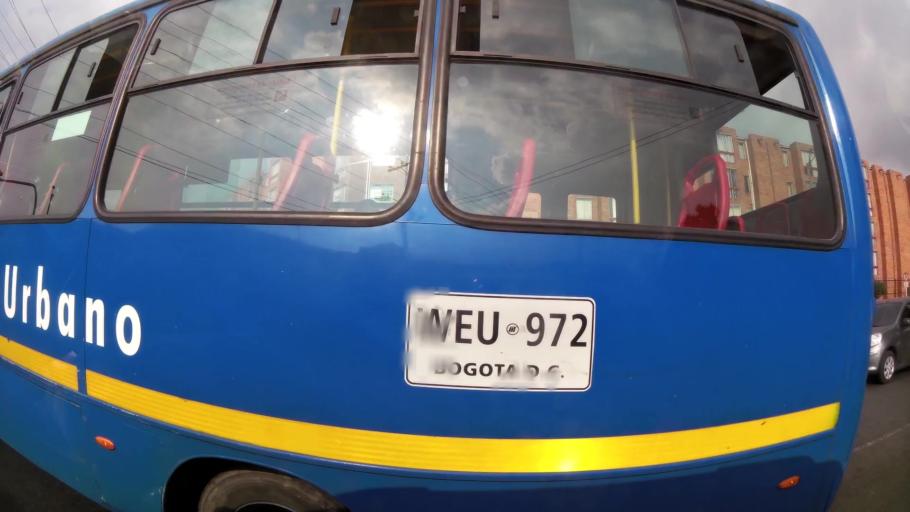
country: CO
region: Bogota D.C.
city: Bogota
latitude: 4.5773
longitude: -74.1291
